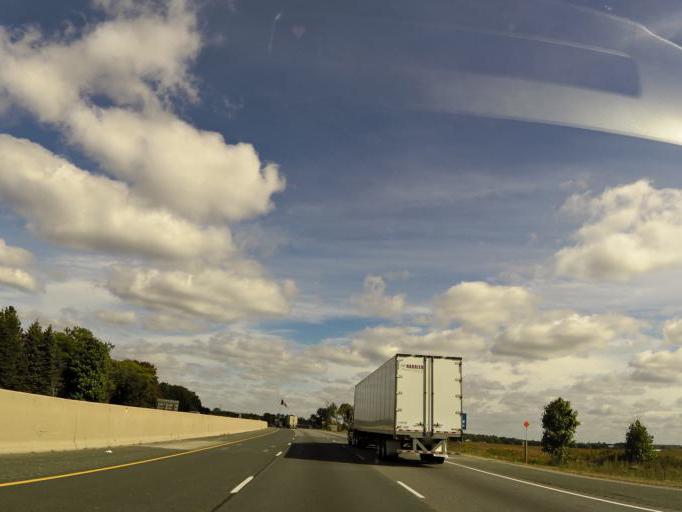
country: CA
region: Ontario
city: Dorchester
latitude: 42.9441
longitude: -81.1152
